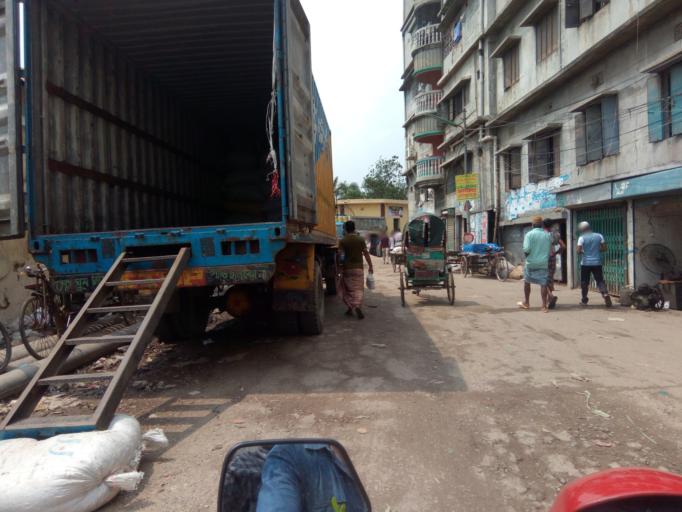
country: BD
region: Dhaka
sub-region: Dhaka
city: Dhaka
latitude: 23.7124
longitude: 90.3914
